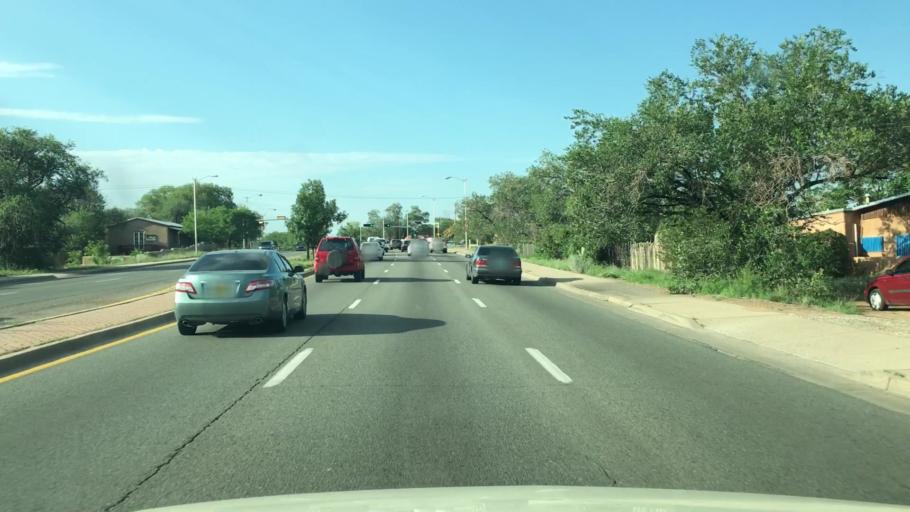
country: US
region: New Mexico
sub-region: Santa Fe County
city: Santa Fe
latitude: 35.6857
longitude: -105.9547
